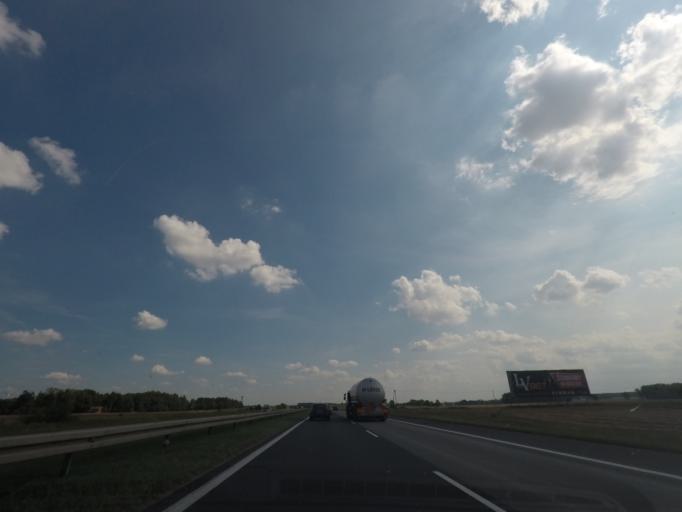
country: PL
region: Lodz Voivodeship
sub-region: Powiat piotrkowski
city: Grabica
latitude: 51.5031
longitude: 19.6053
